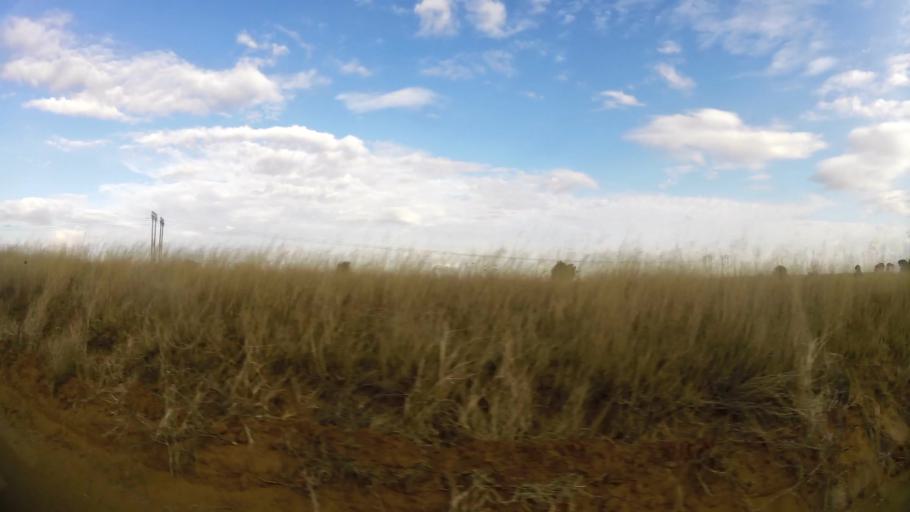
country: ZA
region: Orange Free State
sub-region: Lejweleputswa District Municipality
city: Welkom
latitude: -28.0140
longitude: 26.7210
